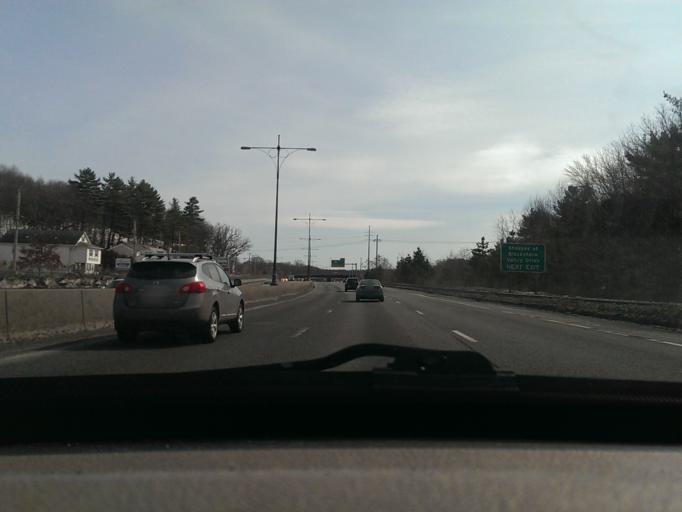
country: US
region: Massachusetts
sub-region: Worcester County
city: Millbury
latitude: 42.2056
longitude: -71.7791
